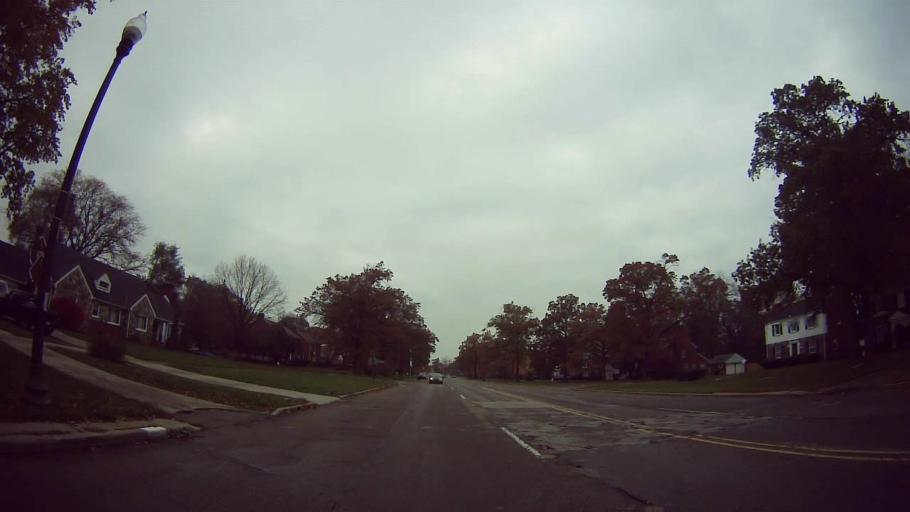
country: US
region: Michigan
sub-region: Oakland County
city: Oak Park
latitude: 42.4348
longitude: -83.1669
